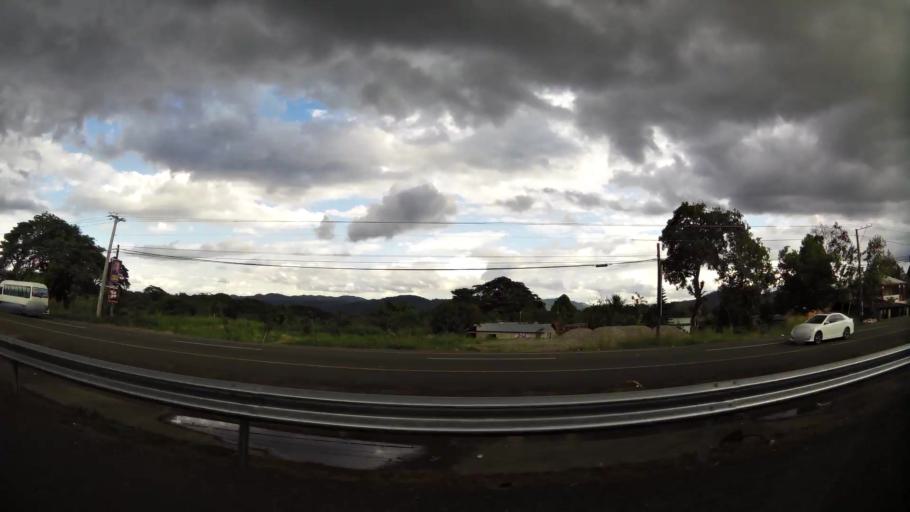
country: DO
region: Monsenor Nouel
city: Sabana del Puerto
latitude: 19.0158
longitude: -70.4451
